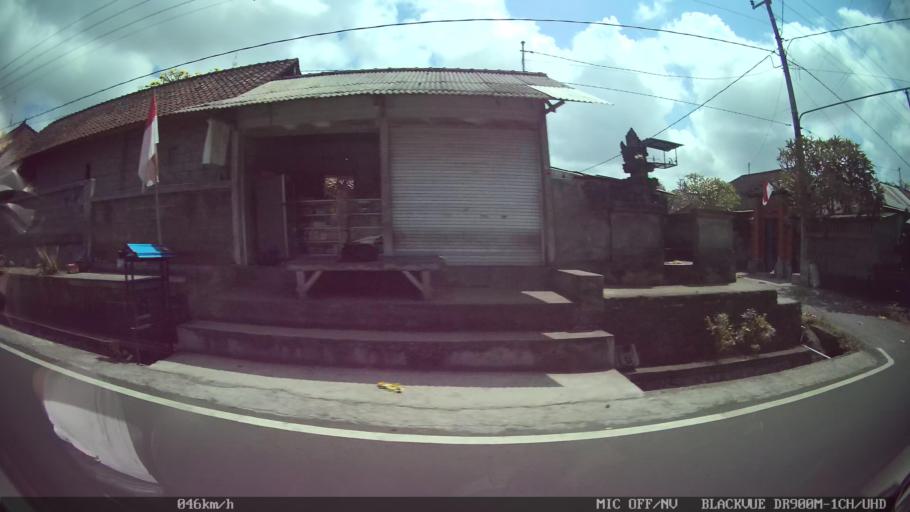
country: ID
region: Bali
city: Banjar Pasekan
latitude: -8.5927
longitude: 115.2985
